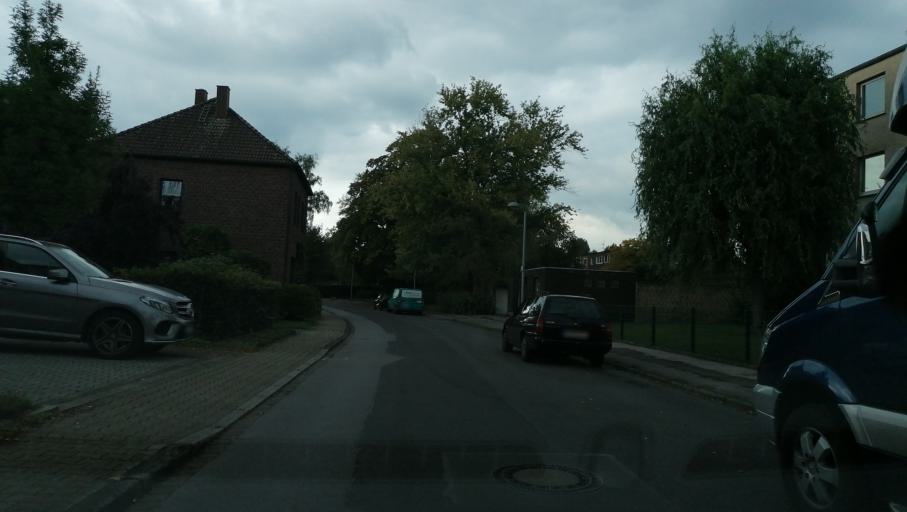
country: DE
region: North Rhine-Westphalia
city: Herten
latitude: 51.5756
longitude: 7.1061
